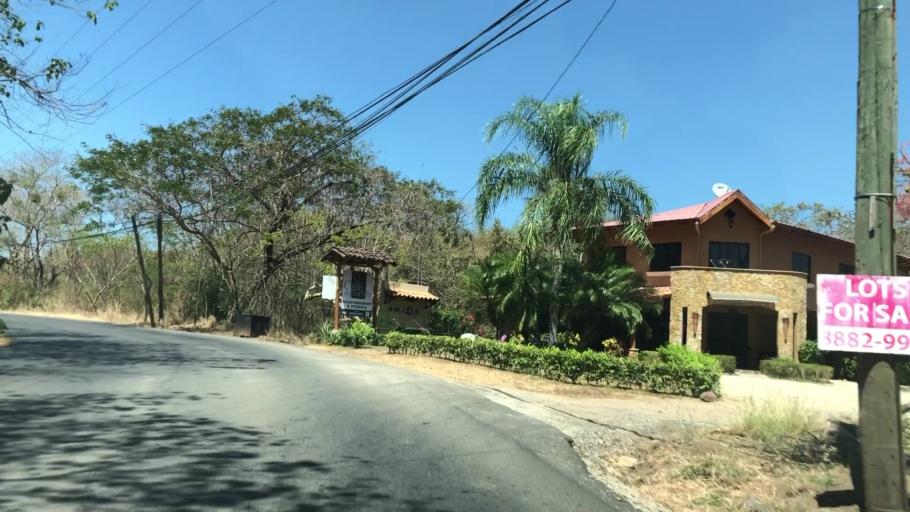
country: CR
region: Guanacaste
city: Sardinal
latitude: 10.3456
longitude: -85.8414
